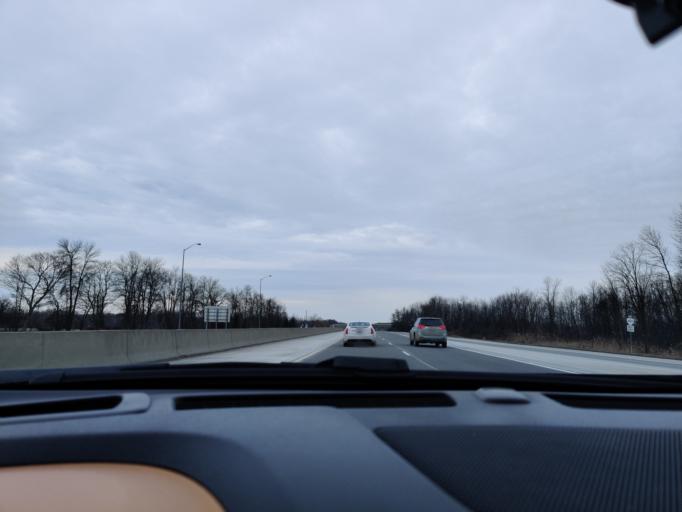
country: CA
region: Ontario
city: Prescott
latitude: 44.7518
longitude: -75.4824
